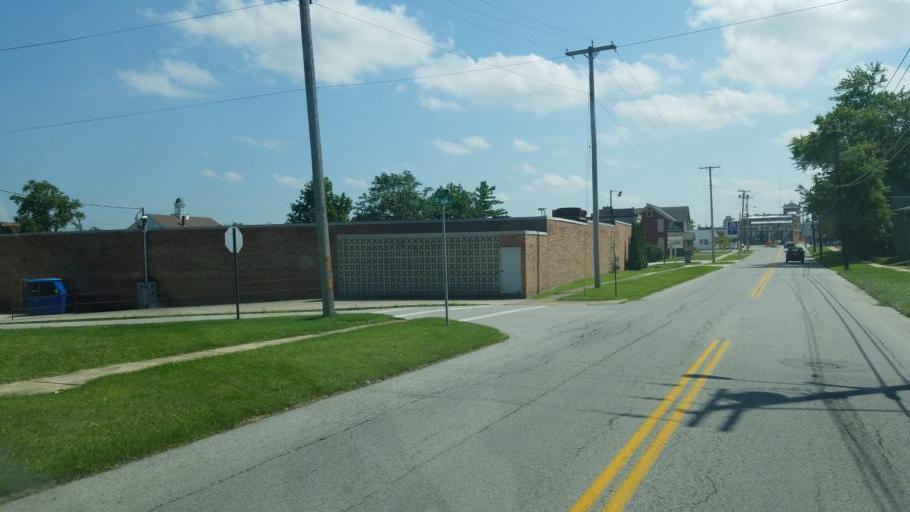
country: US
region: Ohio
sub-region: Huron County
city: Bellevue
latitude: 41.2767
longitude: -82.8402
